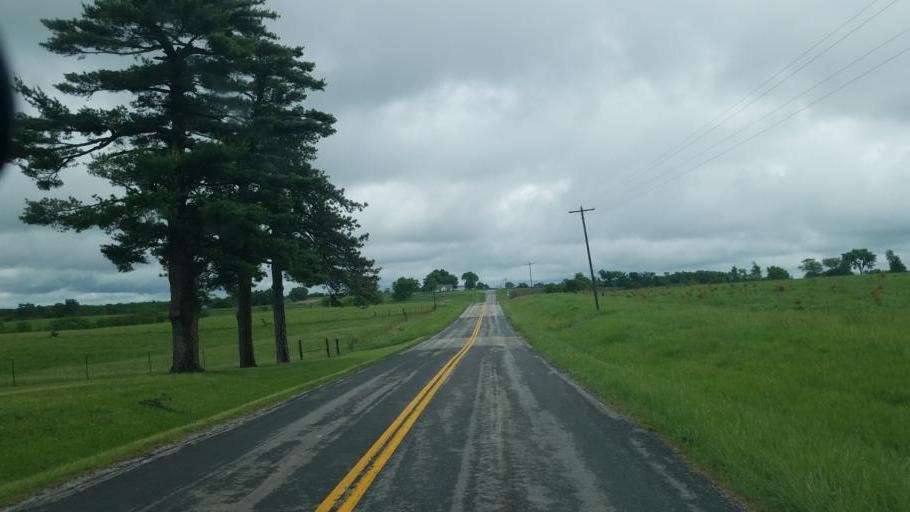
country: US
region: Missouri
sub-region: Mercer County
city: Princeton
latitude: 40.4339
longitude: -93.6847
